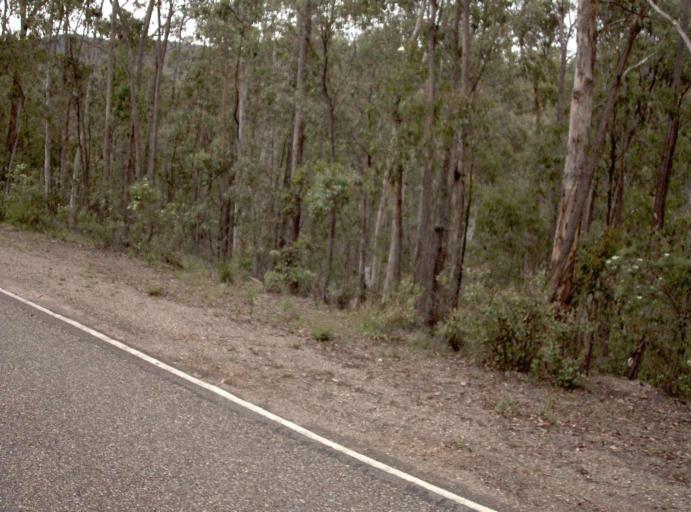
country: AU
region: Victoria
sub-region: East Gippsland
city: Bairnsdale
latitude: -37.6468
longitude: 147.2770
